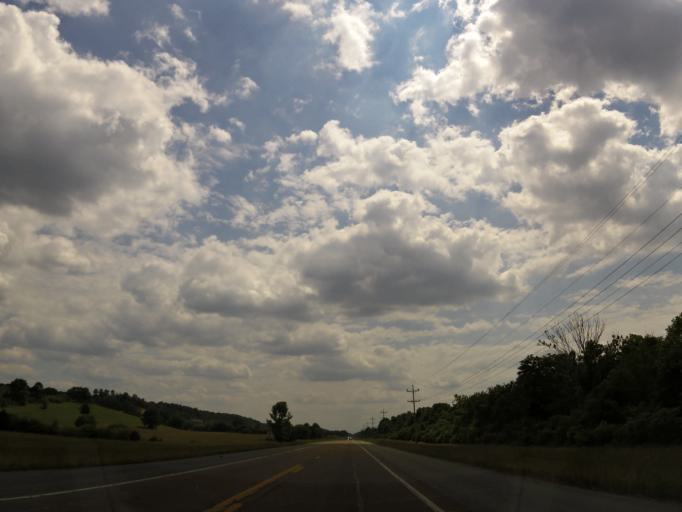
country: US
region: Tennessee
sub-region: Sequatchie County
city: Dunlap
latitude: 35.3348
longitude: -85.4170
